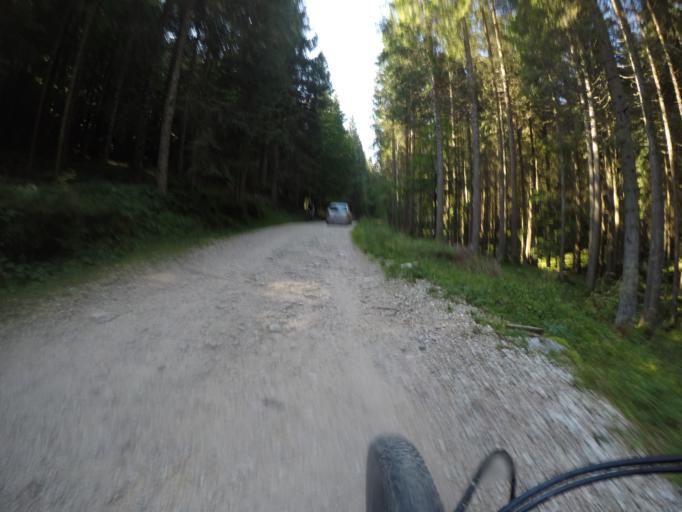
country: IT
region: Veneto
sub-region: Provincia di Vicenza
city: Asiago
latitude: 45.8309
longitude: 11.5100
